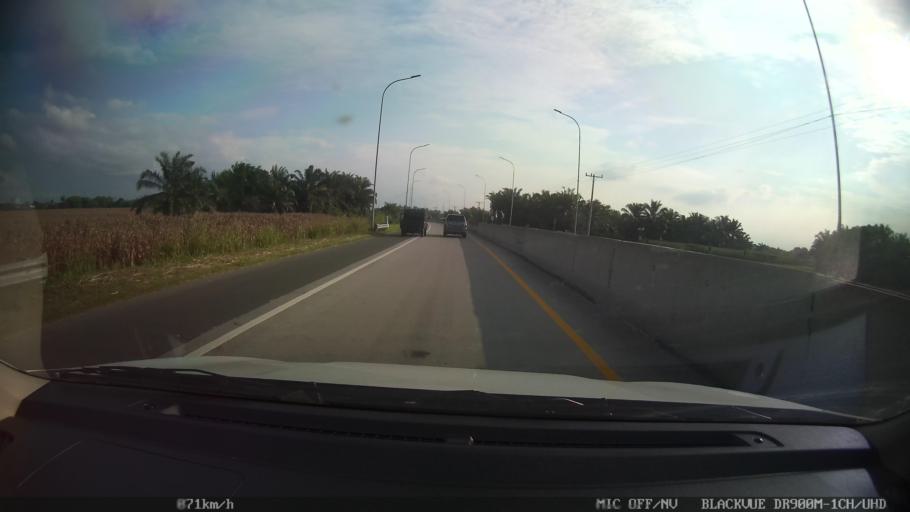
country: ID
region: North Sumatra
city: Sunggal
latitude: 3.6259
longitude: 98.6291
